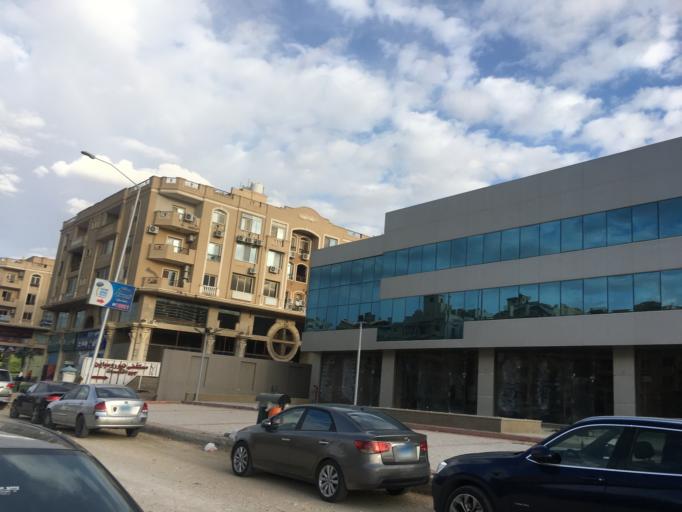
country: EG
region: Al Jizah
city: Madinat Sittah Uktubar
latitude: 29.9722
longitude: 30.9381
